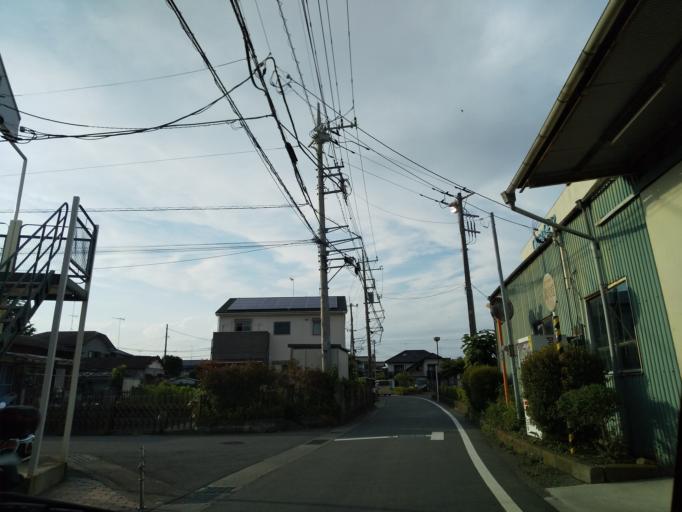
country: JP
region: Kanagawa
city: Zama
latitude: 35.5081
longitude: 139.3614
